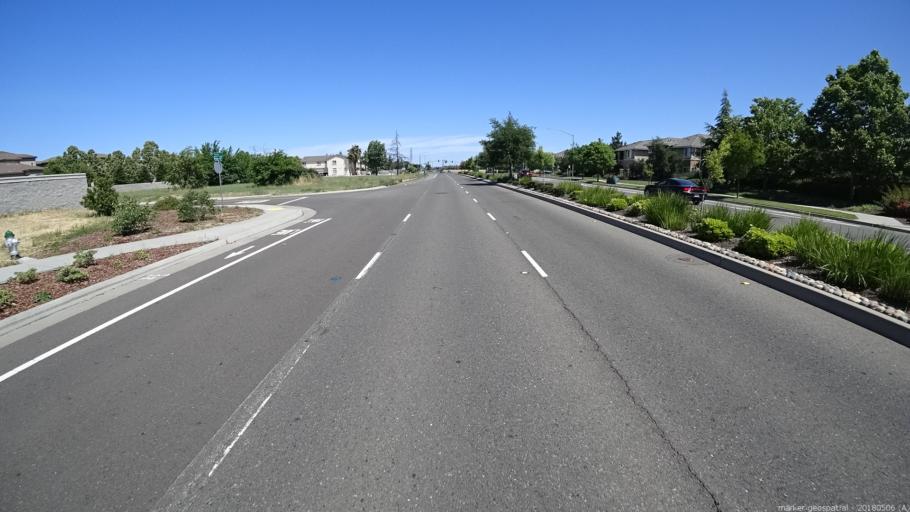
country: US
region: California
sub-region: Sacramento County
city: Laguna
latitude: 38.4449
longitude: -121.4178
